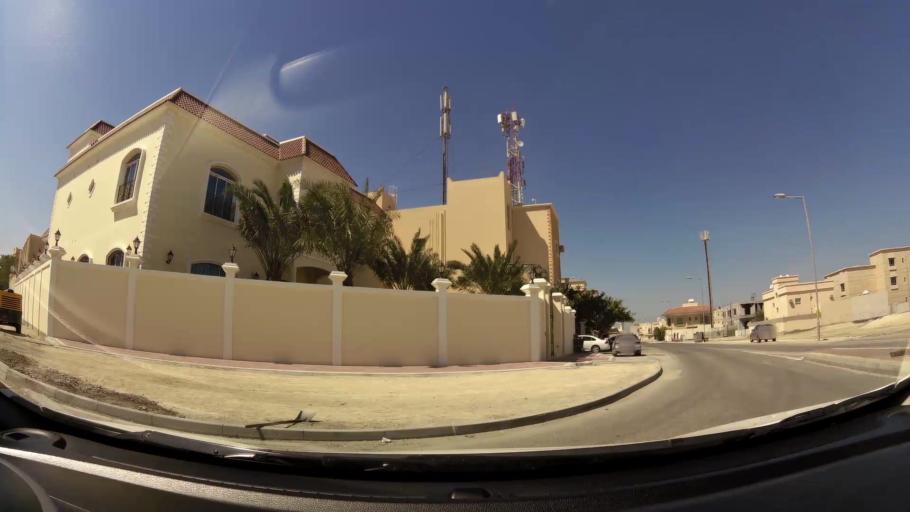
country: BH
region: Muharraq
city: Al Muharraq
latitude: 26.2699
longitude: 50.6018
